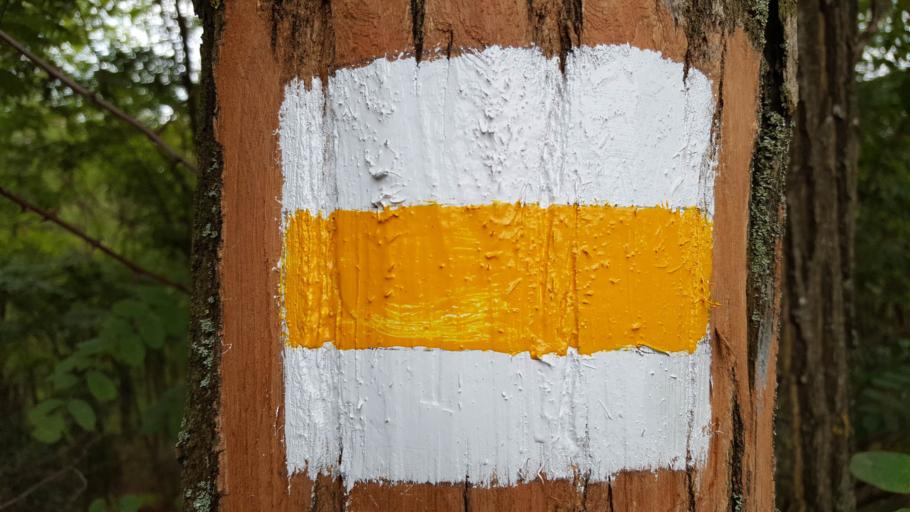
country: HU
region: Somogy
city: Somogyvar
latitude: 46.5339
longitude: 17.6053
